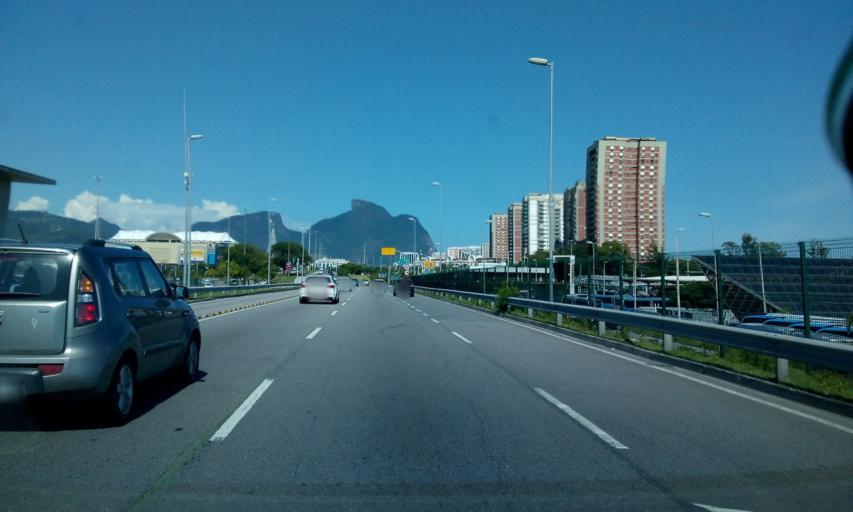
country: BR
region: Rio de Janeiro
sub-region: Rio De Janeiro
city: Rio de Janeiro
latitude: -23.0004
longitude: -43.3667
